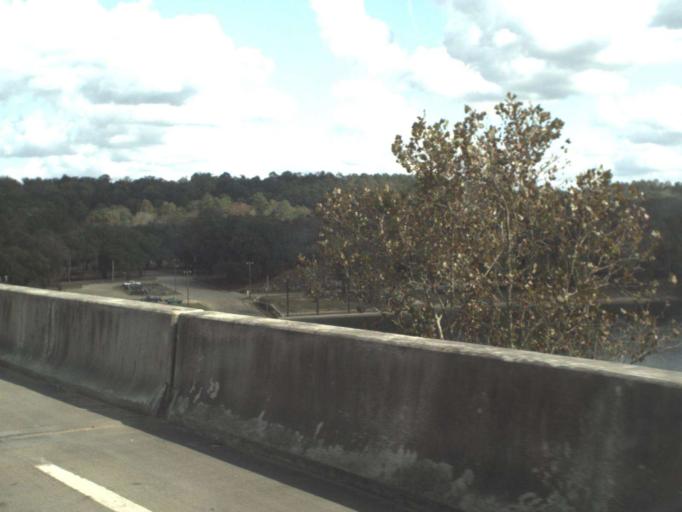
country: US
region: Florida
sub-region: Gadsden County
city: Chattahoochee
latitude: 30.7007
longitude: -84.8602
